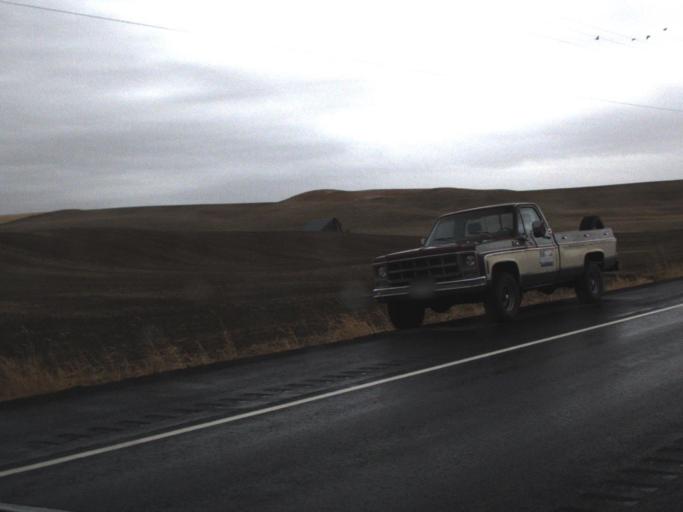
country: US
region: Washington
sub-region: Whitman County
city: Colfax
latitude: 46.8098
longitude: -117.3192
